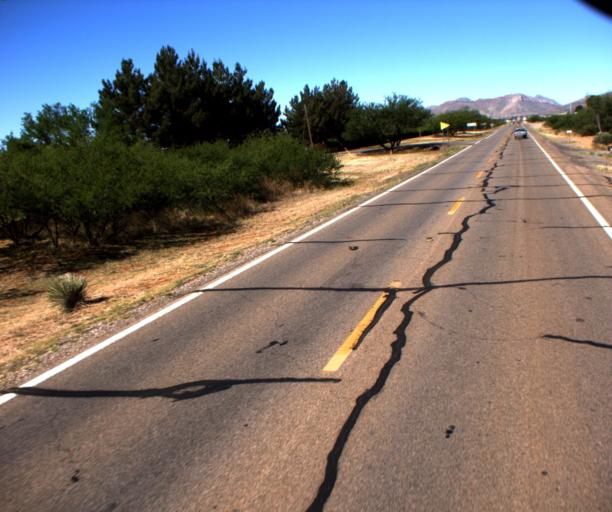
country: US
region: Arizona
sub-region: Cochise County
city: Huachuca City
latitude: 31.6930
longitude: -110.3411
